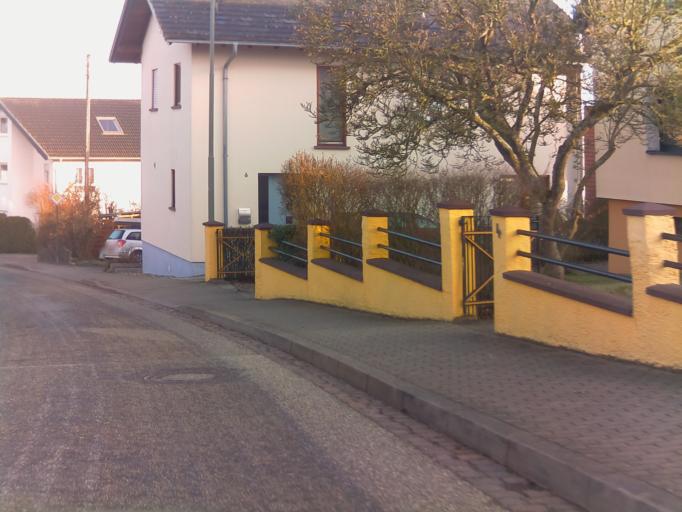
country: DE
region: Rheinland-Pfalz
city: Bruchmuhlbach-Miesau
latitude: 49.4153
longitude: 7.4340
